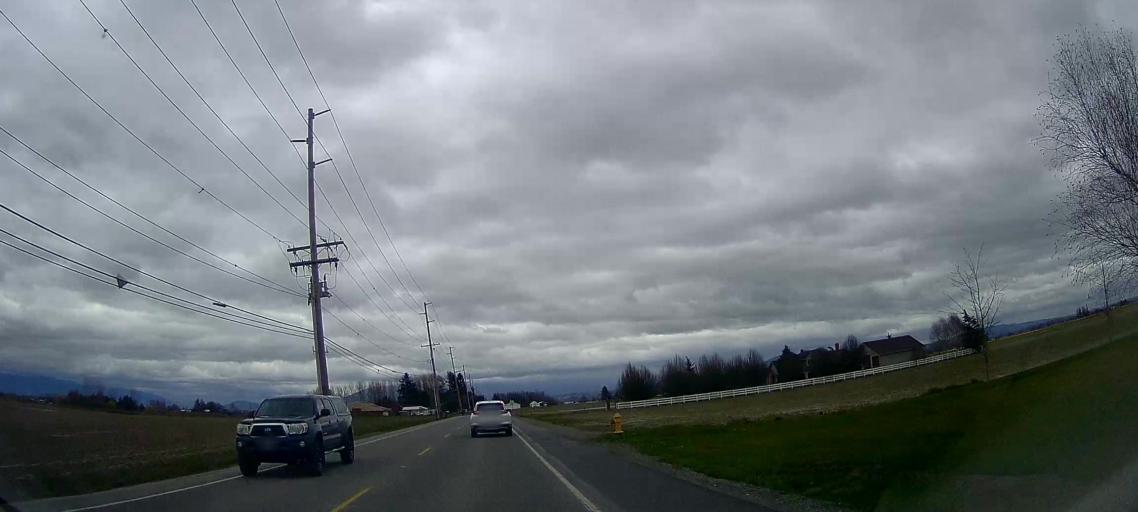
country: US
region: Washington
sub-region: Skagit County
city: Mount Vernon
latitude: 48.4211
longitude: -122.4402
